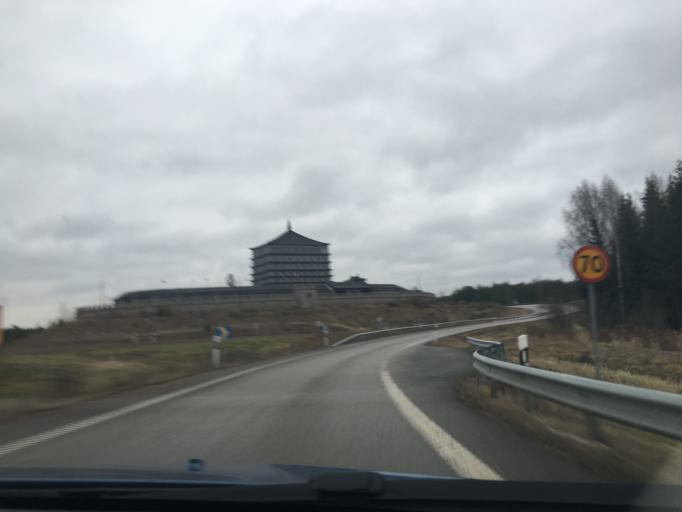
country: SE
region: Uppsala
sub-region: Alvkarleby Kommun
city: AElvkarleby
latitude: 60.4605
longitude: 17.4148
